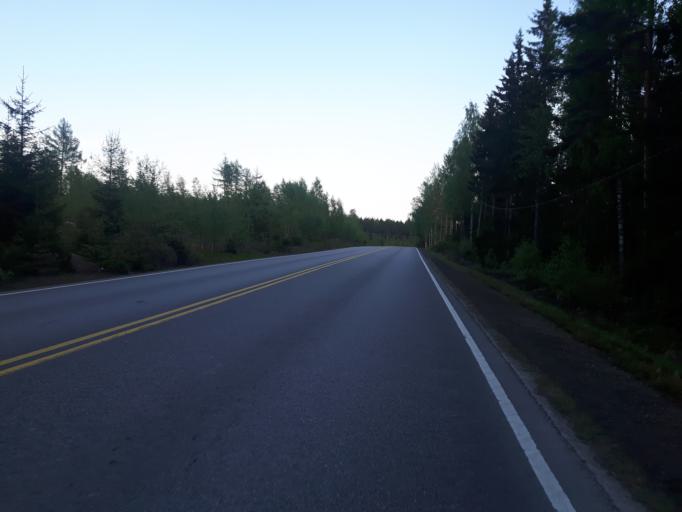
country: FI
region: Uusimaa
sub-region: Loviisa
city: Perna
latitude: 60.4565
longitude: 26.0826
